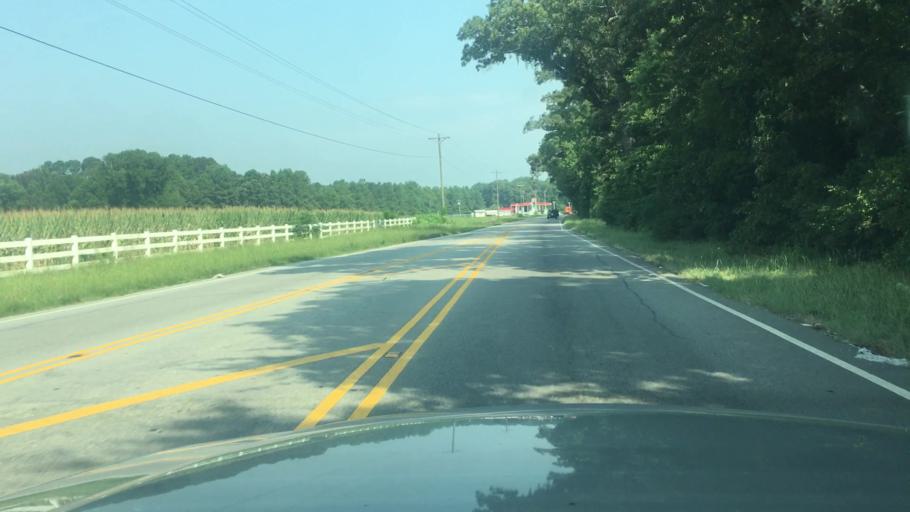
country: US
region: North Carolina
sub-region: Cumberland County
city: Hope Mills
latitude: 34.9319
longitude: -78.9170
